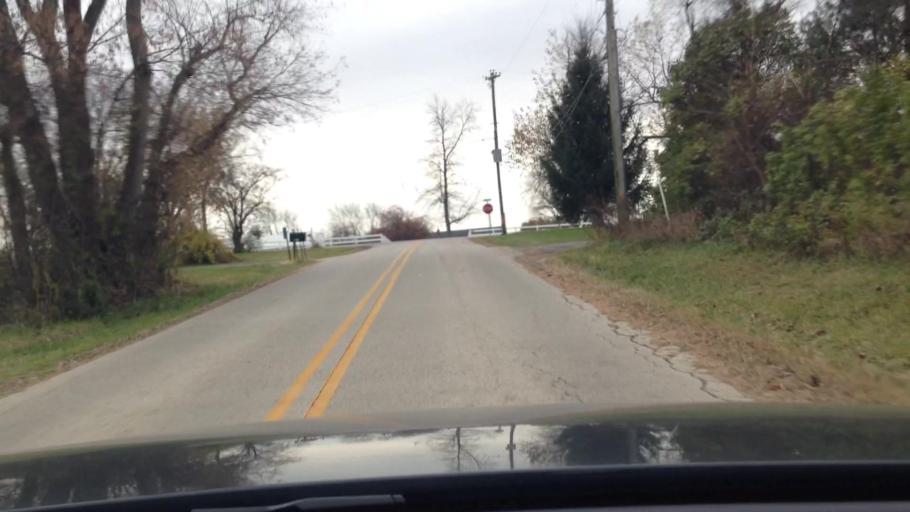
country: US
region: Illinois
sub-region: McHenry County
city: Woodstock
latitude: 42.2774
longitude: -88.4770
